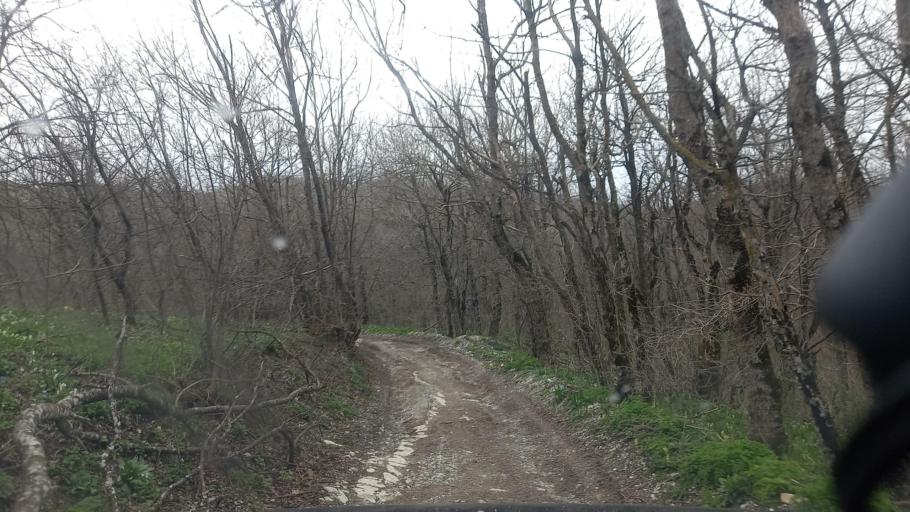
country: RU
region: Krasnodarskiy
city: Gelendzhik
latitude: 44.6144
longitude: 38.2057
